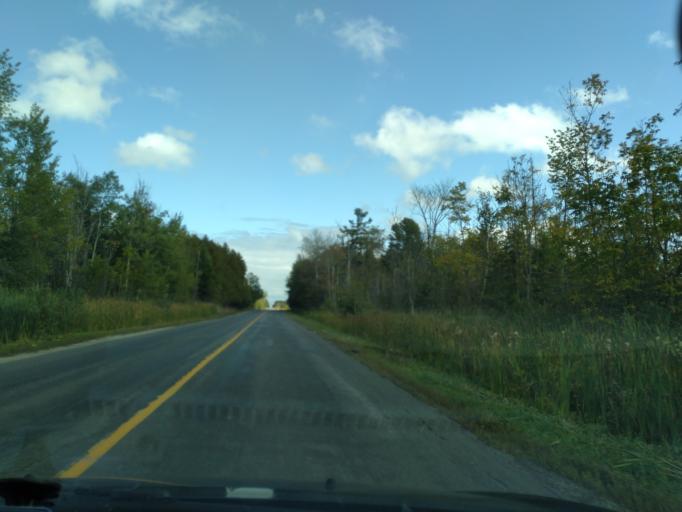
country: CA
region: Ontario
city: Innisfil
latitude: 44.2807
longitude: -79.5878
